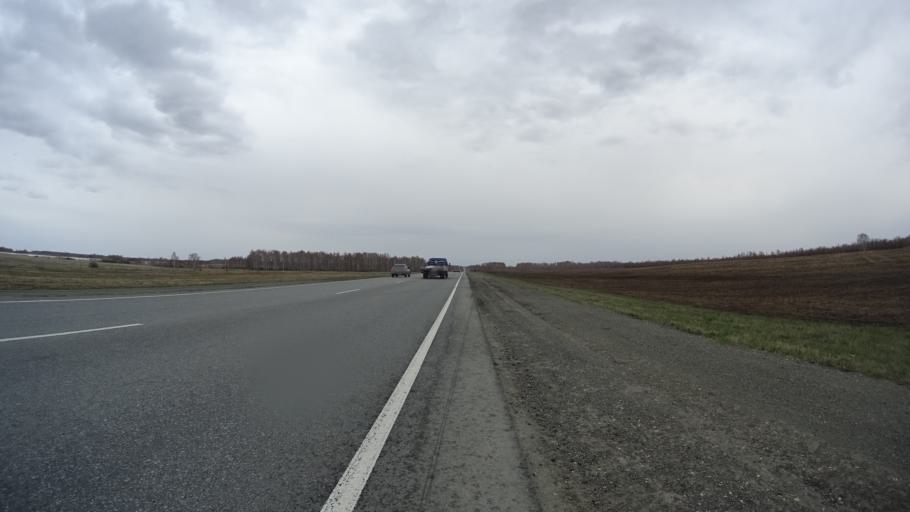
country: RU
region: Chelyabinsk
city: Krasnogorskiy
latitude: 54.6634
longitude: 61.2538
